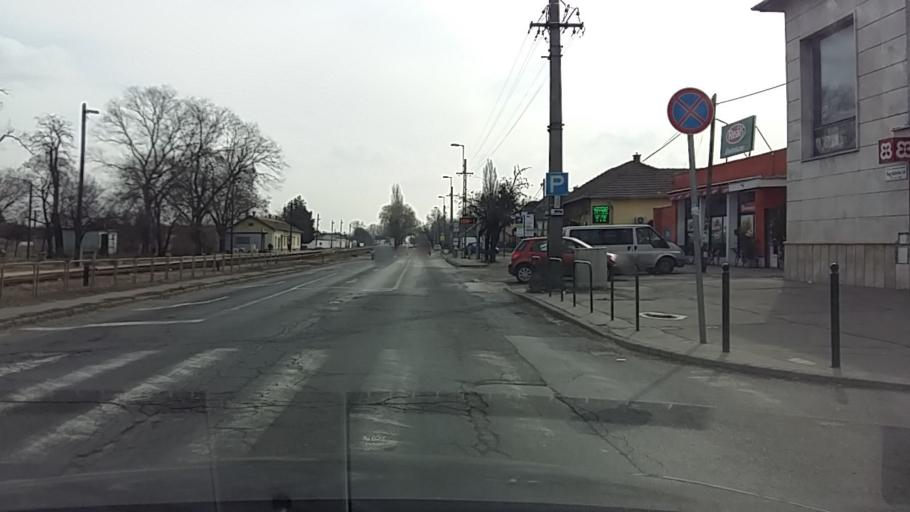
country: HU
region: Pest
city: Gyal
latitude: 47.4038
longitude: 19.1861
